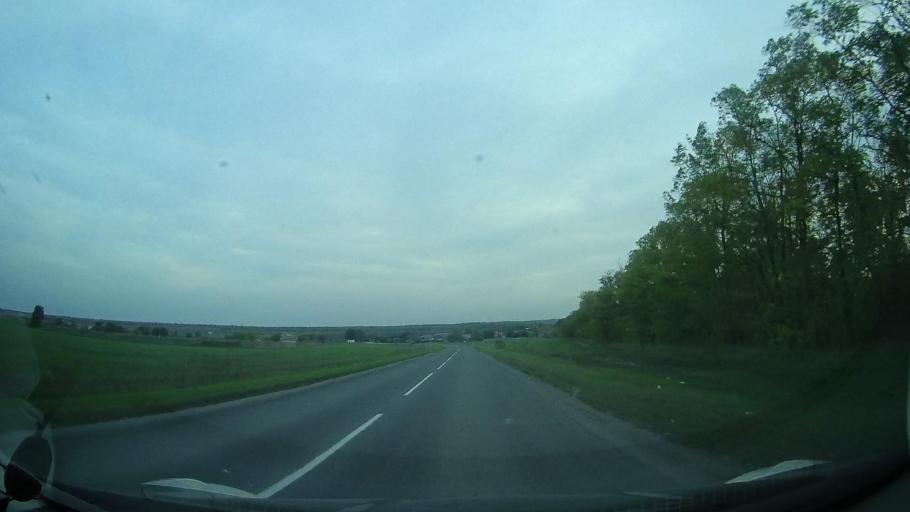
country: RU
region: Rostov
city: Kirovskaya
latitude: 47.0396
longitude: 39.9778
